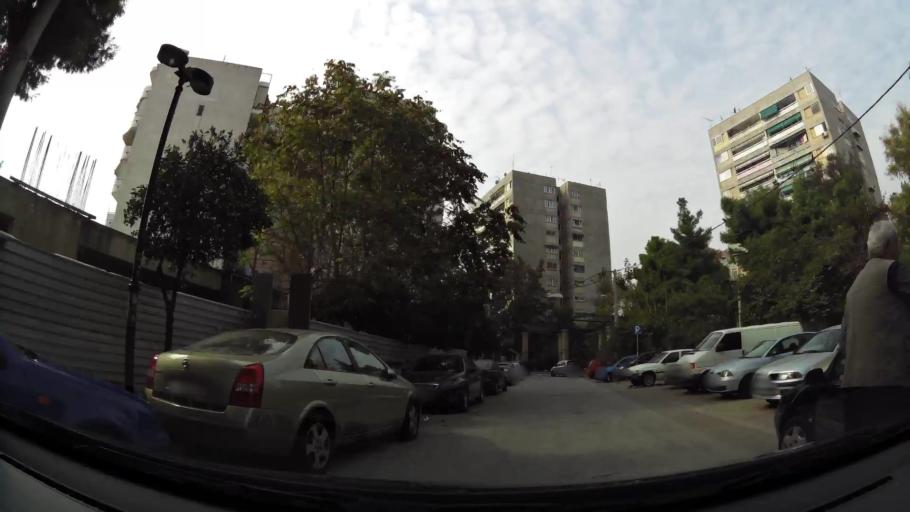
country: GR
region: Attica
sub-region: Nomarchia Athinas
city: Tavros
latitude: 37.9663
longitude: 23.6992
